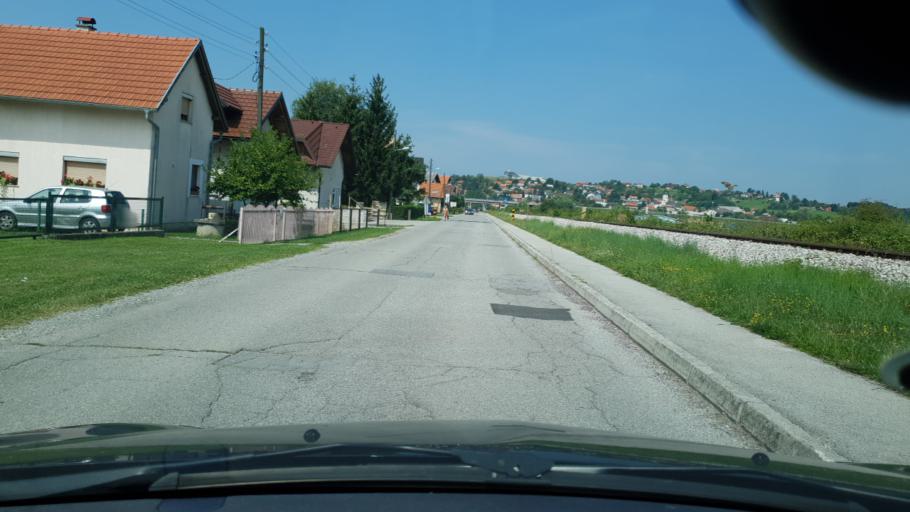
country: HR
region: Krapinsko-Zagorska
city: Zabok
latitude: 46.0233
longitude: 15.9205
